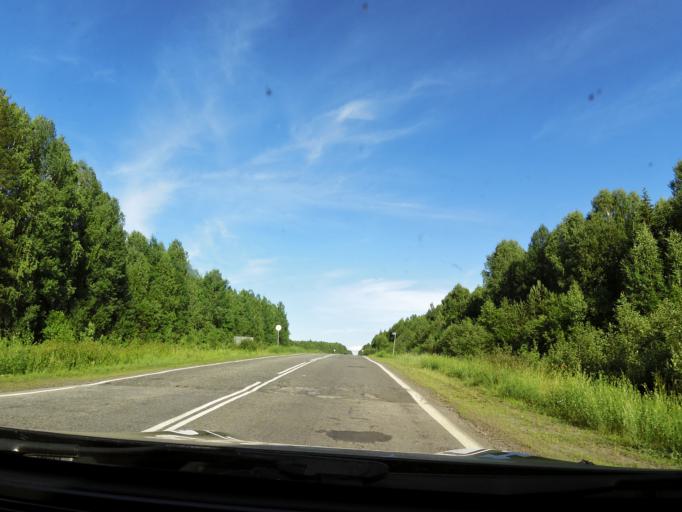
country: RU
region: Kirov
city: Chernaya Kholunitsa
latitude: 58.8902
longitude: 51.3560
